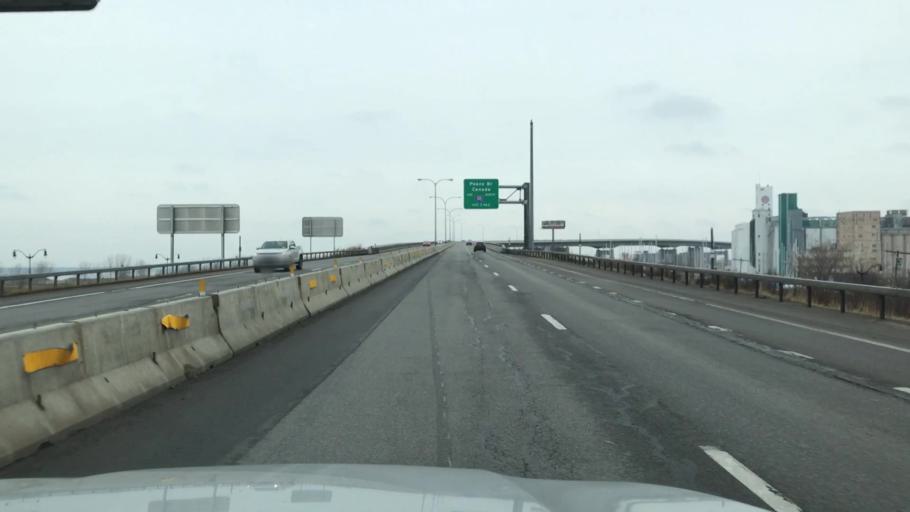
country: US
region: New York
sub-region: Erie County
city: Buffalo
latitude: 42.8661
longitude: -78.8762
